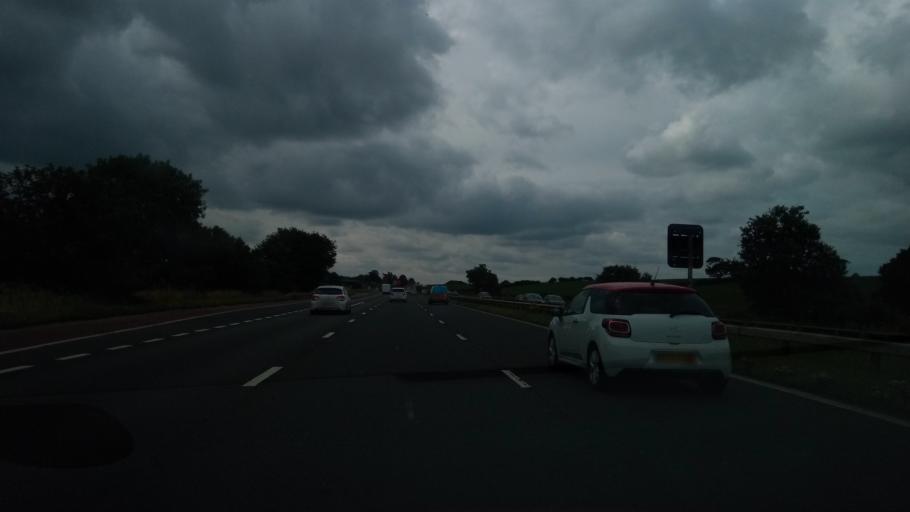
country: GB
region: England
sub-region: Lancashire
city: Galgate
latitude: 53.9891
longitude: -2.7812
